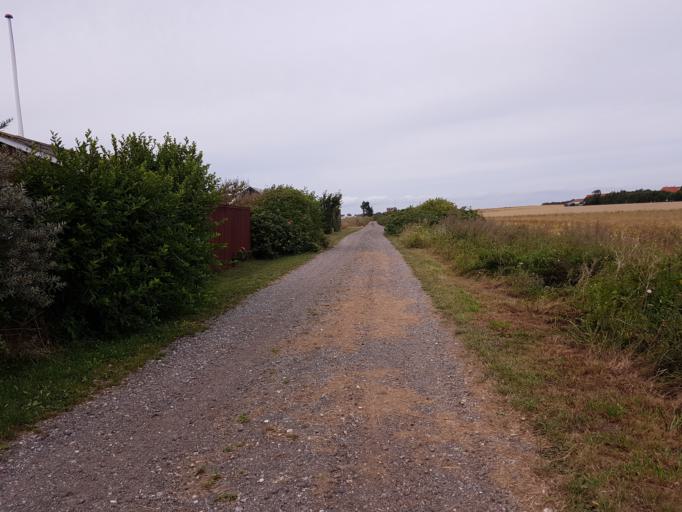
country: DK
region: Zealand
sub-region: Guldborgsund Kommune
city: Nykobing Falster
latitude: 54.5864
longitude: 11.9226
